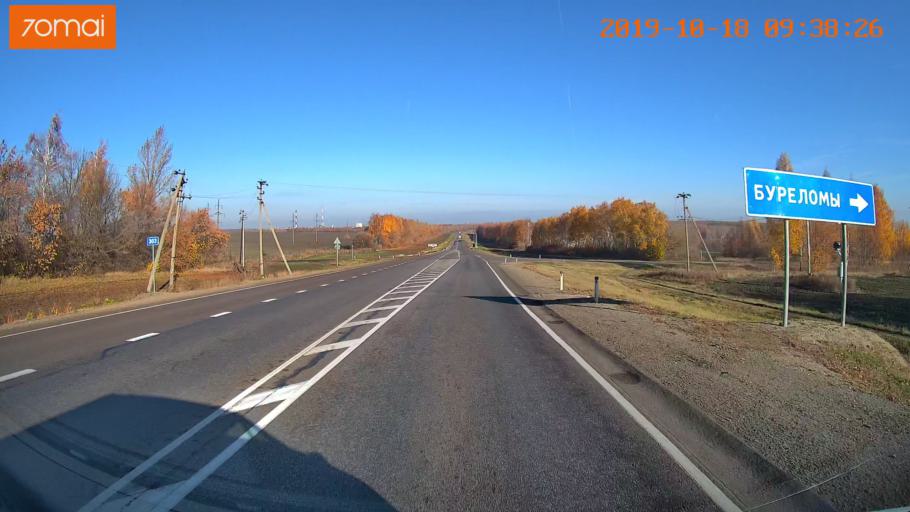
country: RU
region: Tula
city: Yefremov
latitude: 53.2380
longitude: 38.1371
